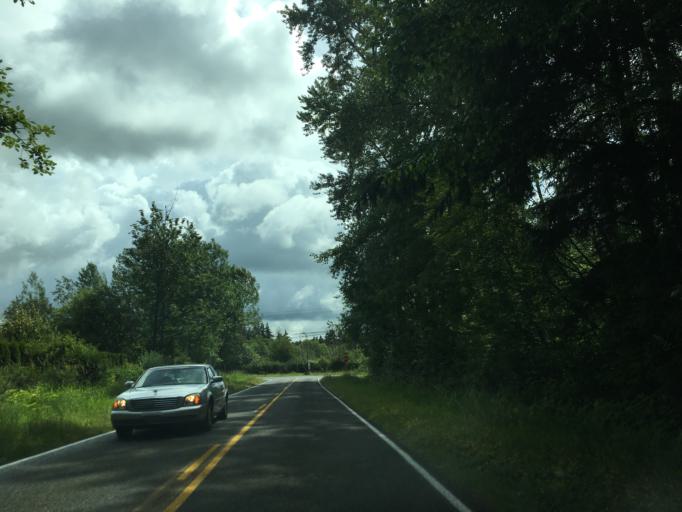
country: US
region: Washington
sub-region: Whatcom County
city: Birch Bay
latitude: 48.9032
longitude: -122.7499
